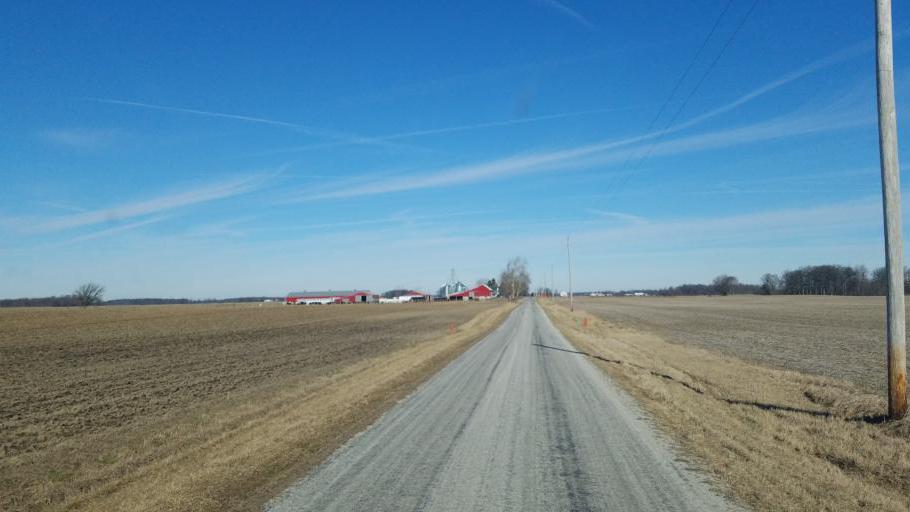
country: US
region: Ohio
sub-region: Union County
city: Richwood
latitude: 40.5235
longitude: -83.4096
